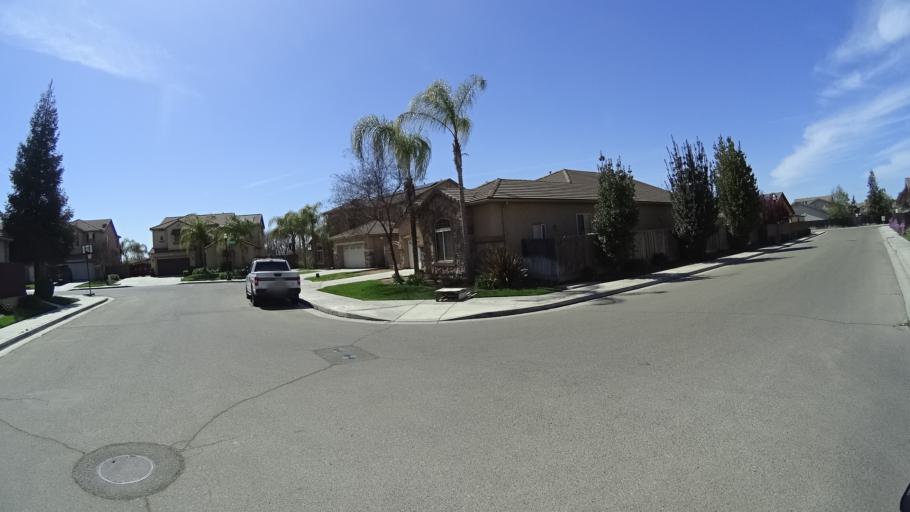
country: US
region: California
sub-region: Fresno County
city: Biola
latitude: 36.8178
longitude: -119.9100
